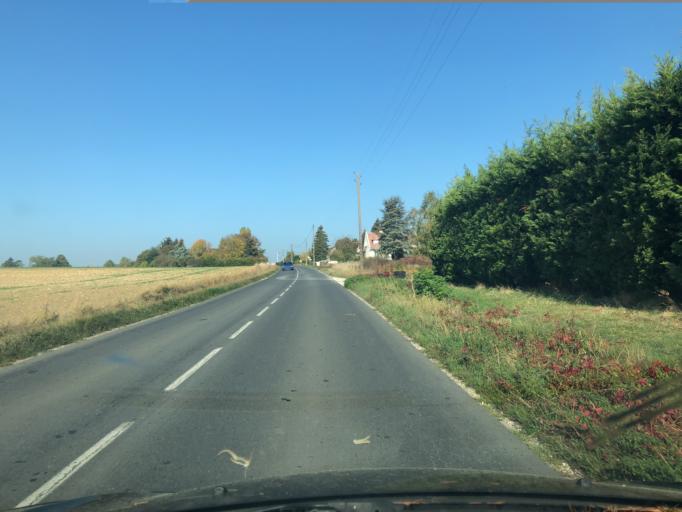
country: FR
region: Centre
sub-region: Departement d'Indre-et-Loire
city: Mettray
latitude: 47.4480
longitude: 0.6756
